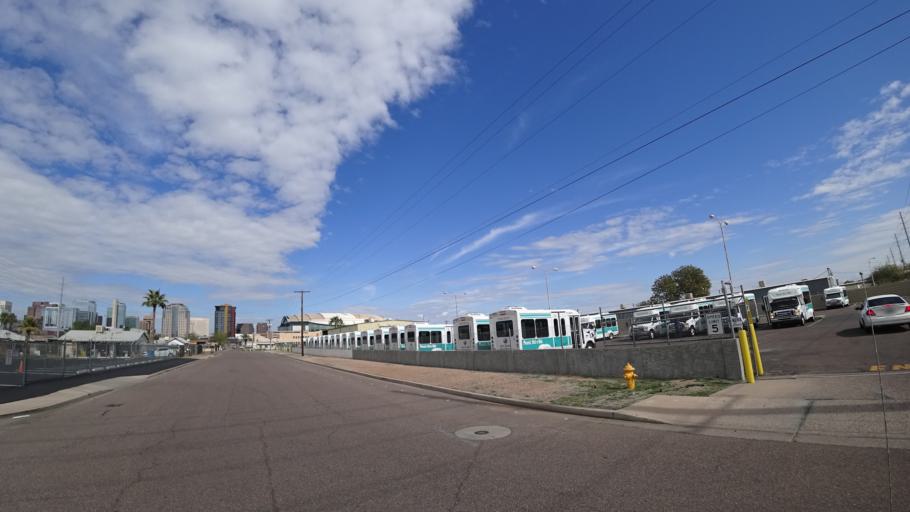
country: US
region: Arizona
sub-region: Maricopa County
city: Phoenix
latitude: 33.4380
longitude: -112.0687
